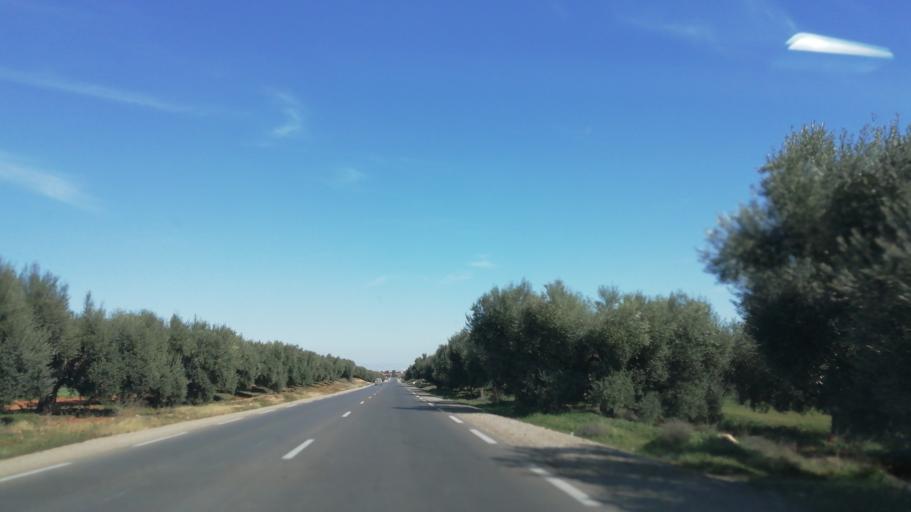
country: DZ
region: Mascara
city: Oued el Abtal
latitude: 35.4200
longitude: 0.4326
